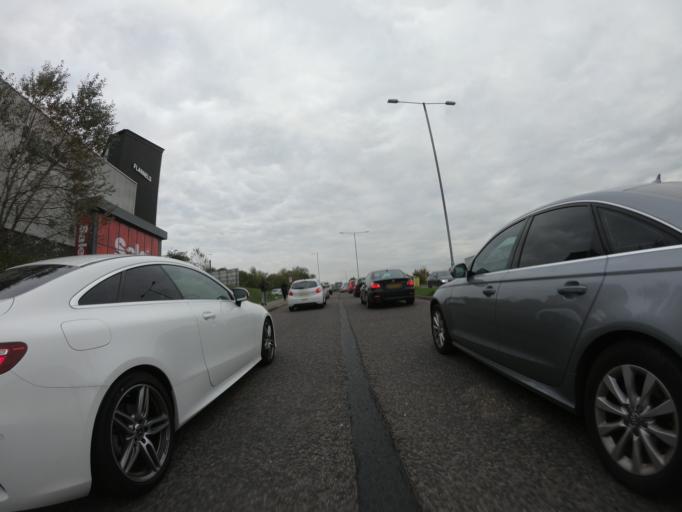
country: GB
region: England
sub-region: Kent
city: West Thurrock
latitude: 51.4853
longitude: 0.2725
